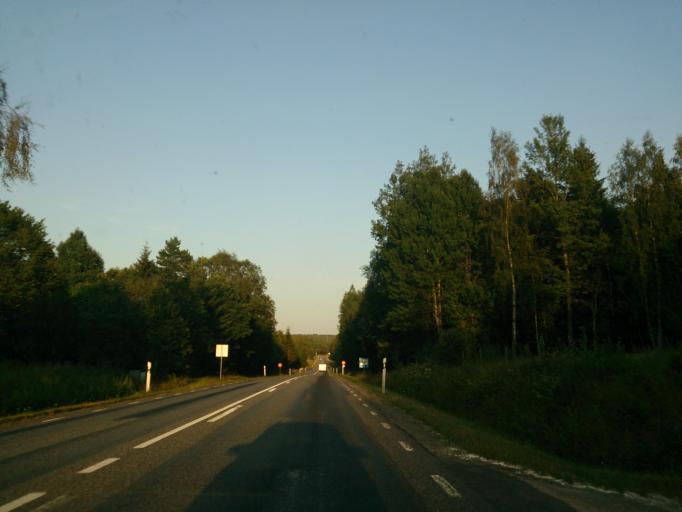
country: SE
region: Joenkoeping
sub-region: Varnamo Kommun
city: Bor
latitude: 57.1242
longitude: 14.1446
